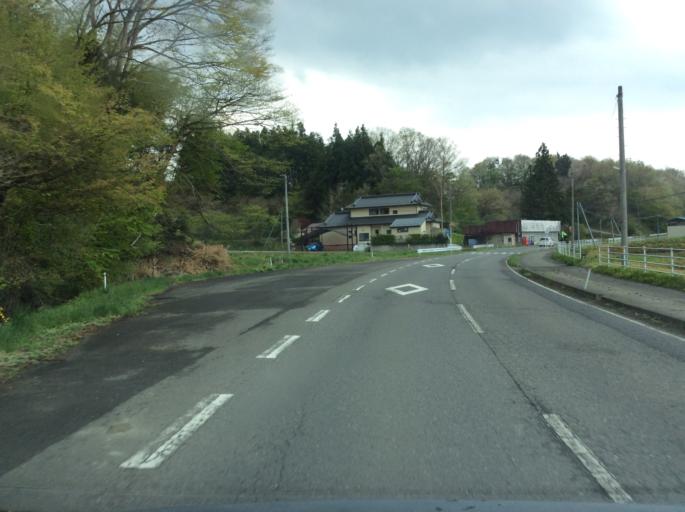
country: JP
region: Fukushima
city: Funehikimachi-funehiki
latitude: 37.4055
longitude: 140.5406
